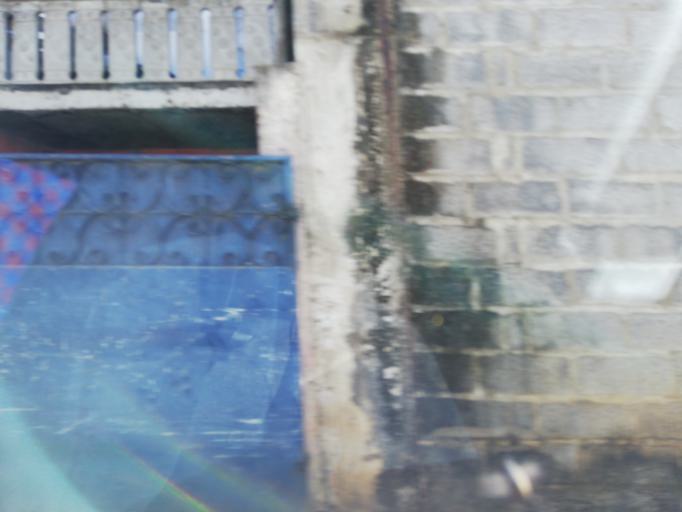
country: MU
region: Moka
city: Moka
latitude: -20.2174
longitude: 57.4670
